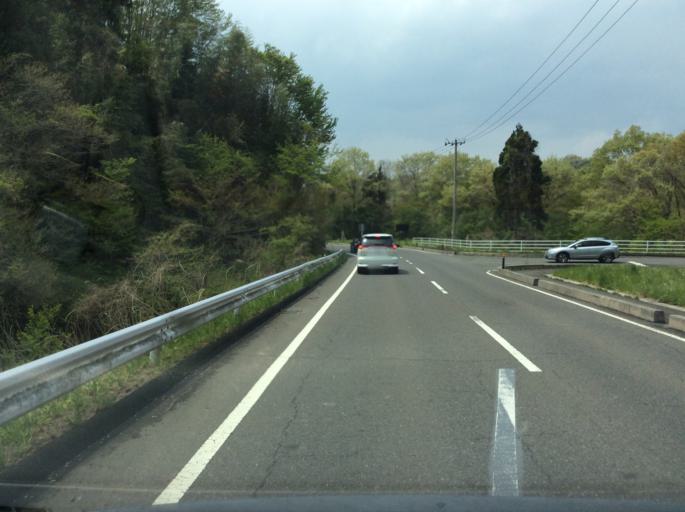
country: JP
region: Fukushima
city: Miharu
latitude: 37.4009
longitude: 140.4732
